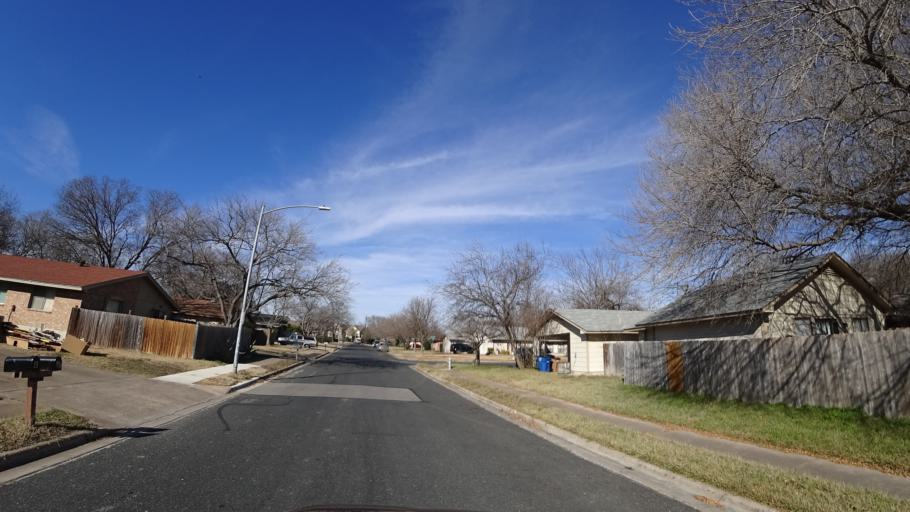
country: US
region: Texas
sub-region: Travis County
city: Wells Branch
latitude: 30.3805
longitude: -97.7016
